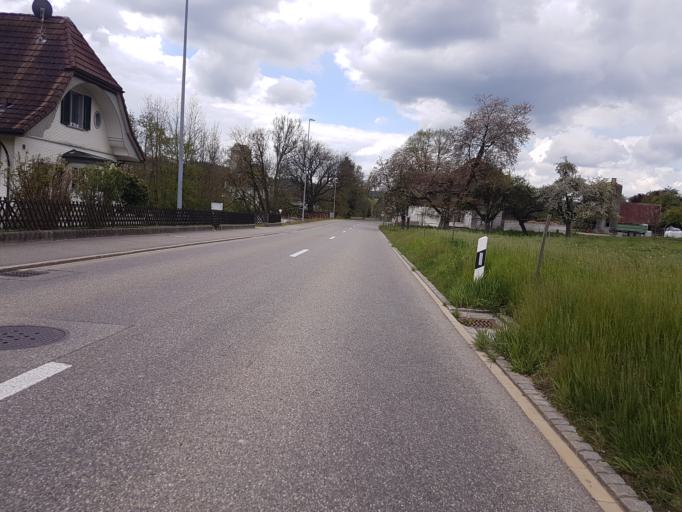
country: CH
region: Bern
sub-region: Oberaargau
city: Aarwangen
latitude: 47.2485
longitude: 7.7646
